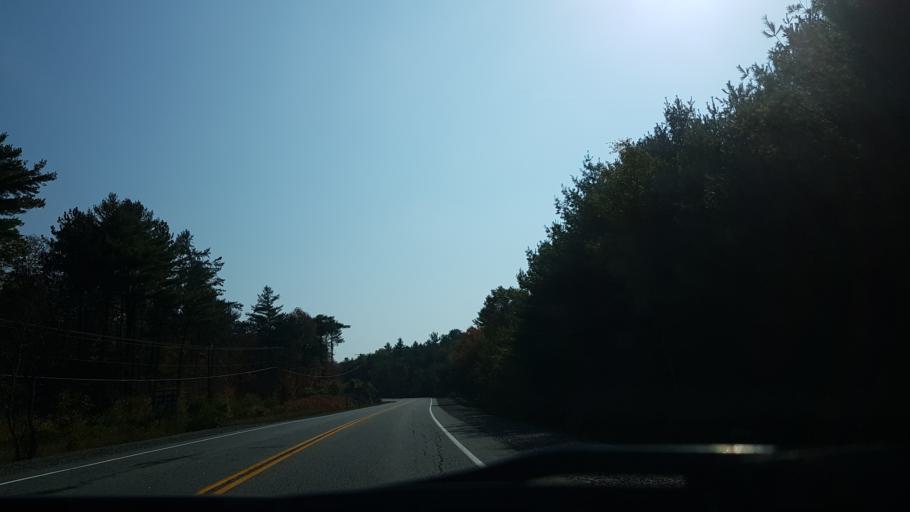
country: CA
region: Ontario
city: Bracebridge
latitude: 44.9844
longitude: -79.2684
